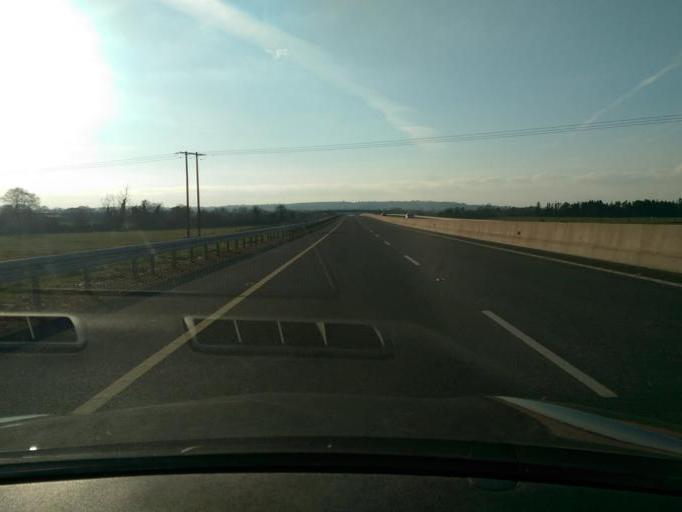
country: IE
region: Munster
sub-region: North Tipperary
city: Roscrea
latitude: 52.9243
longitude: -7.7391
